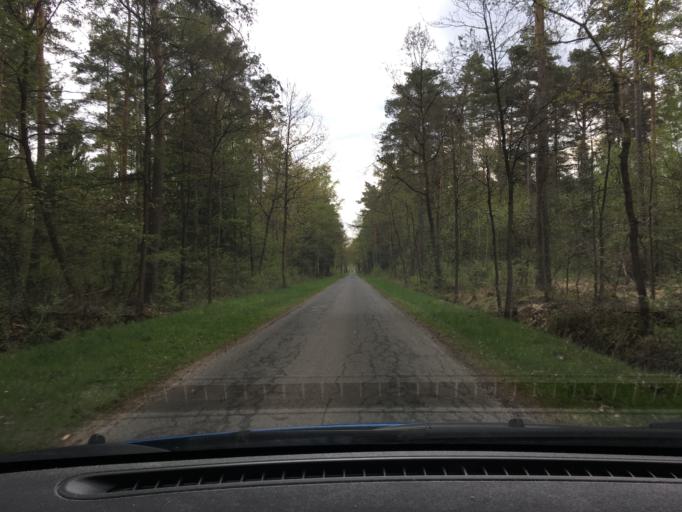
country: DE
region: Lower Saxony
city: Radbruch
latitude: 53.2841
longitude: 10.2598
